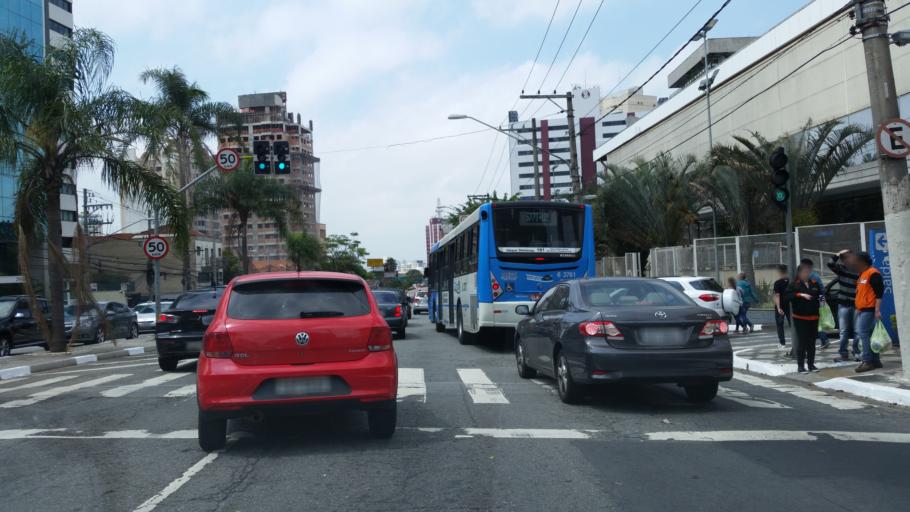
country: BR
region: Sao Paulo
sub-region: Diadema
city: Diadema
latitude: -23.6290
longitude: -46.6452
